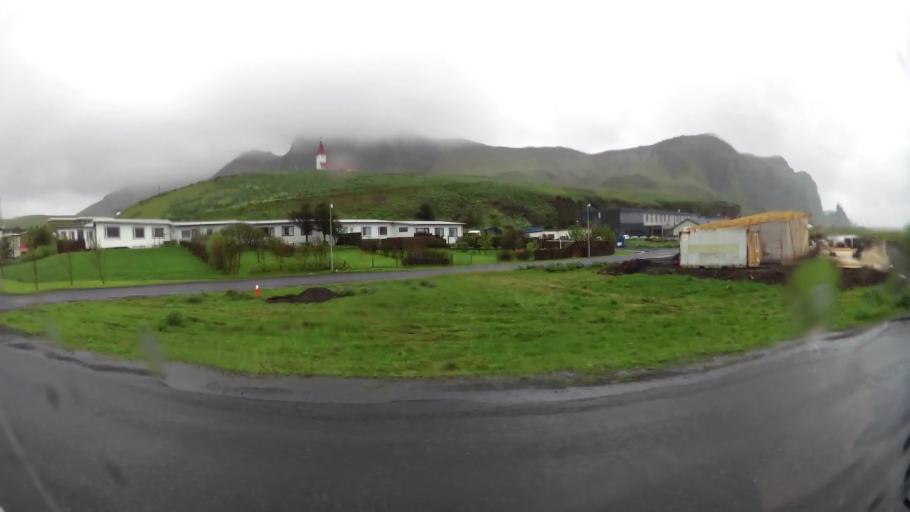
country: IS
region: South
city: Vestmannaeyjar
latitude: 63.4186
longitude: -19.0041
